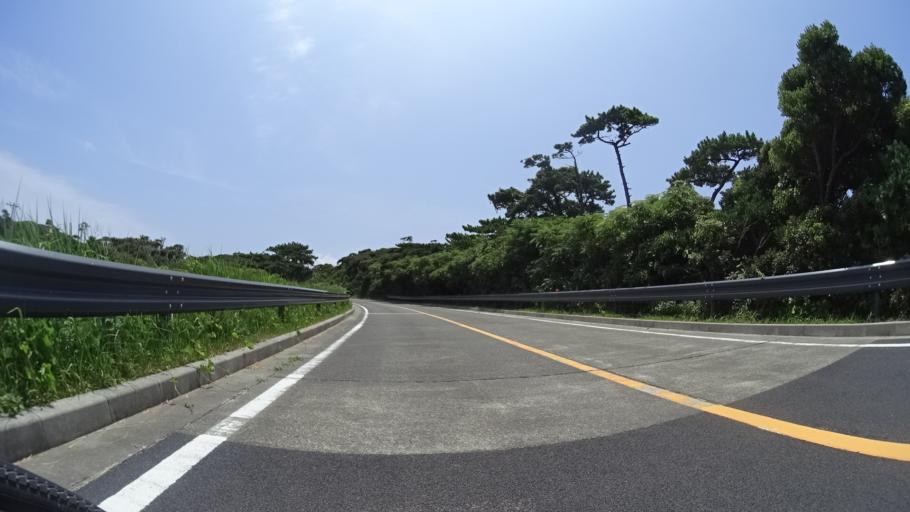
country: JP
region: Shizuoka
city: Shimoda
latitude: 34.3271
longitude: 139.2082
